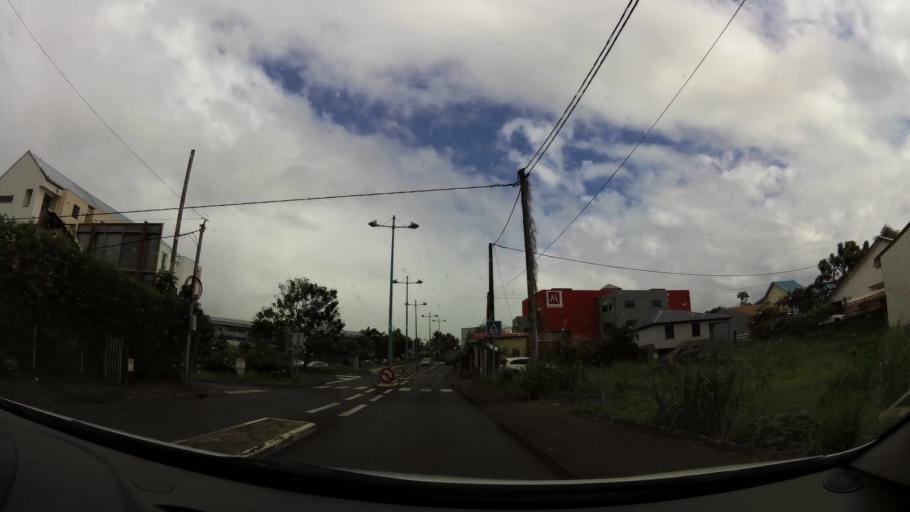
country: RE
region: Reunion
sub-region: Reunion
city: Sainte-Suzanne
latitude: -20.9040
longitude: 55.6008
